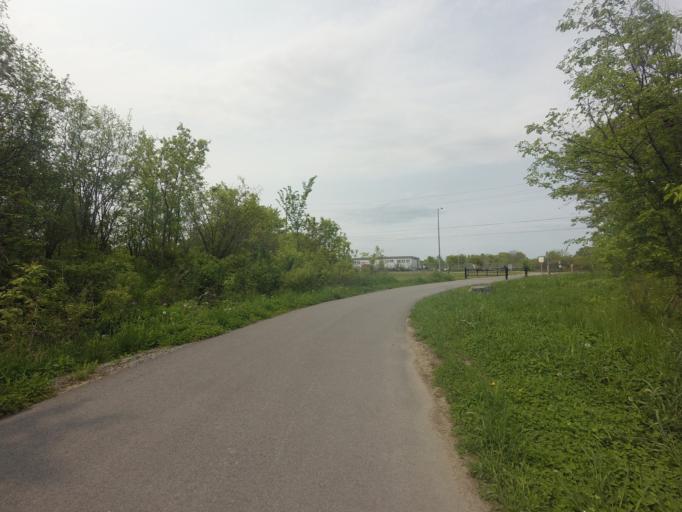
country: CA
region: Ontario
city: Kingston
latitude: 44.2563
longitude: -76.4922
